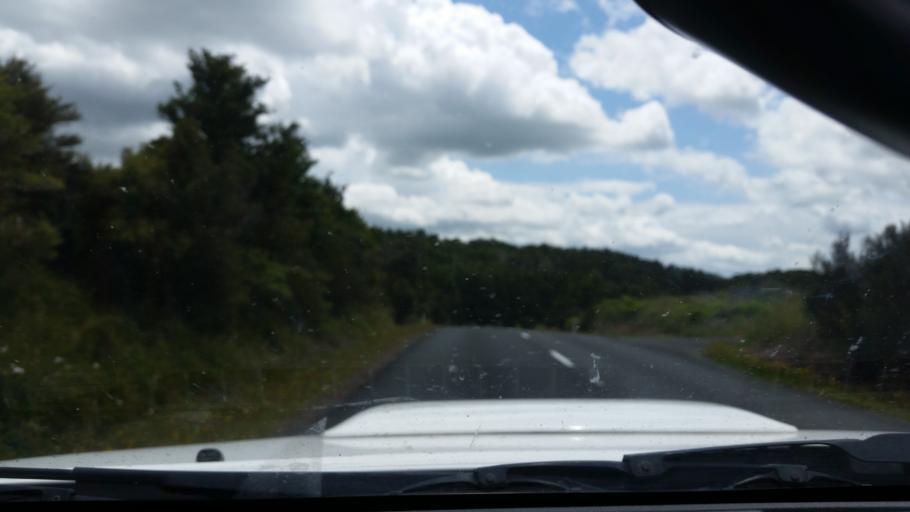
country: NZ
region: Northland
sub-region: Kaipara District
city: Dargaville
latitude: -35.8716
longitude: 173.8432
